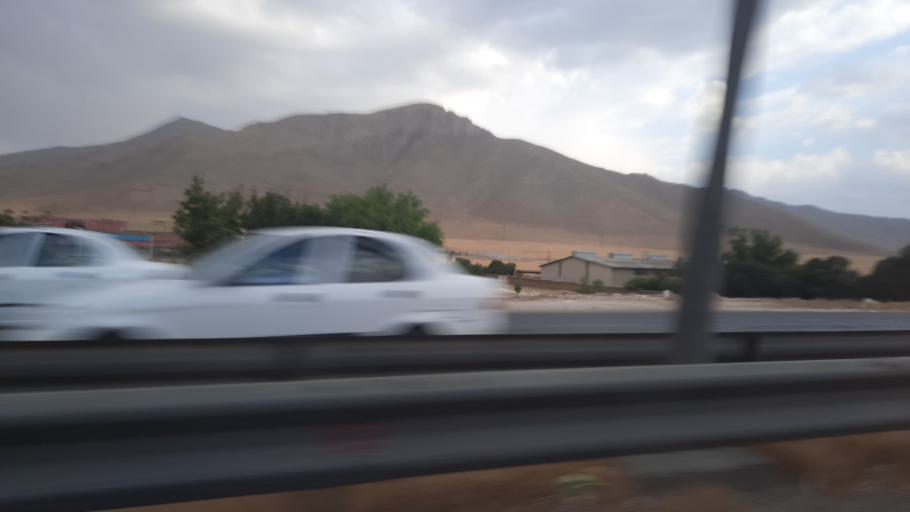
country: IR
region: Markazi
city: Arak
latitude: 34.0153
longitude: 49.5506
